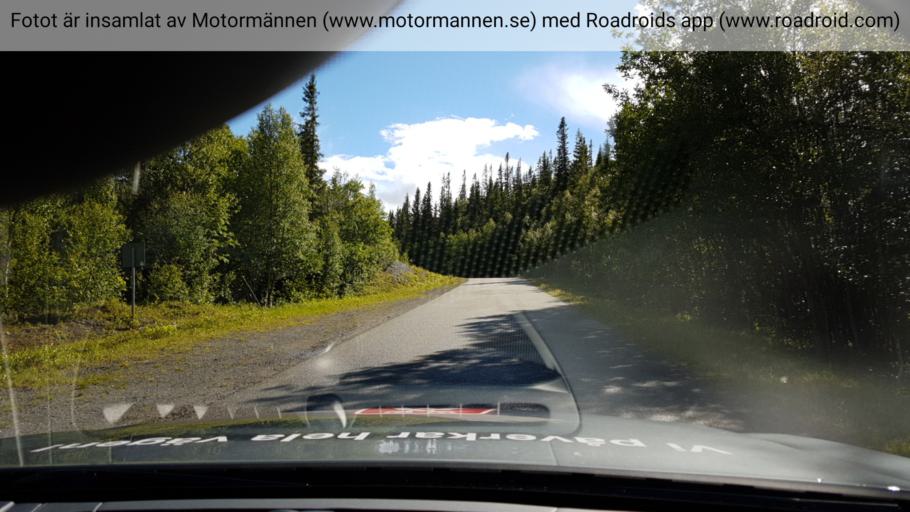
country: SE
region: Jaemtland
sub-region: Bergs Kommun
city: Hoverberg
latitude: 63.0158
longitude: 13.9437
